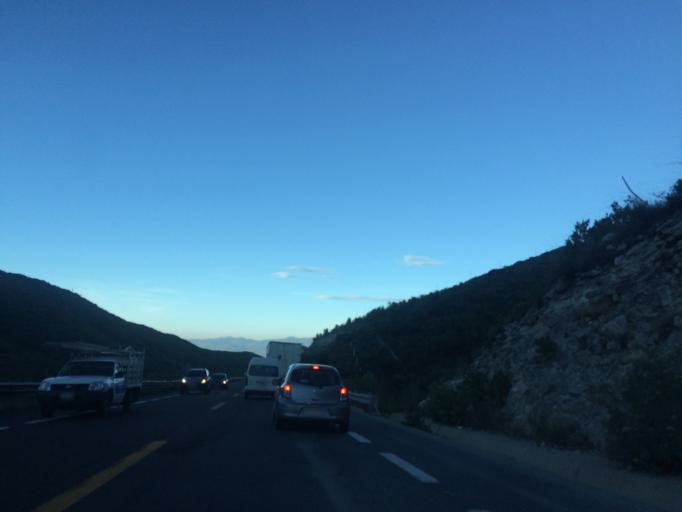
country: MX
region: Puebla
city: Chapuco
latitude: 18.6409
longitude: -97.4580
